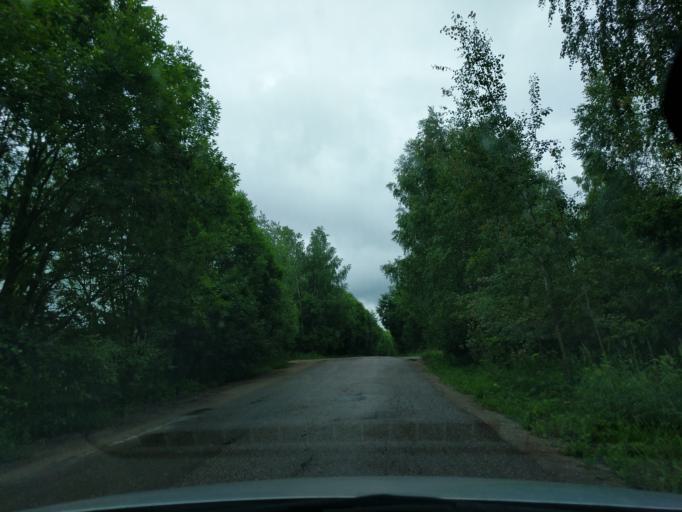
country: RU
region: Kaluga
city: Myatlevo
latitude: 54.8527
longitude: 35.5948
